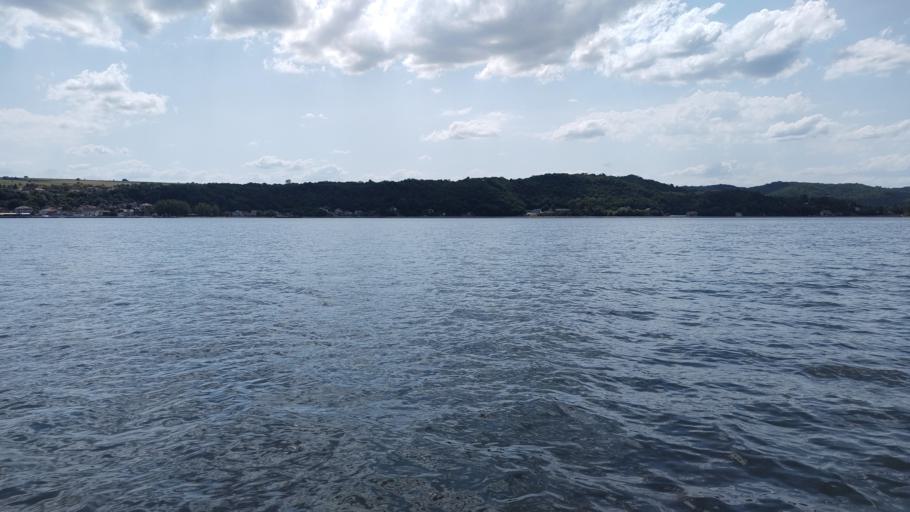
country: RS
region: Central Serbia
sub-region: Branicevski Okrug
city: Golubac
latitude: 44.6601
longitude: 21.6333
